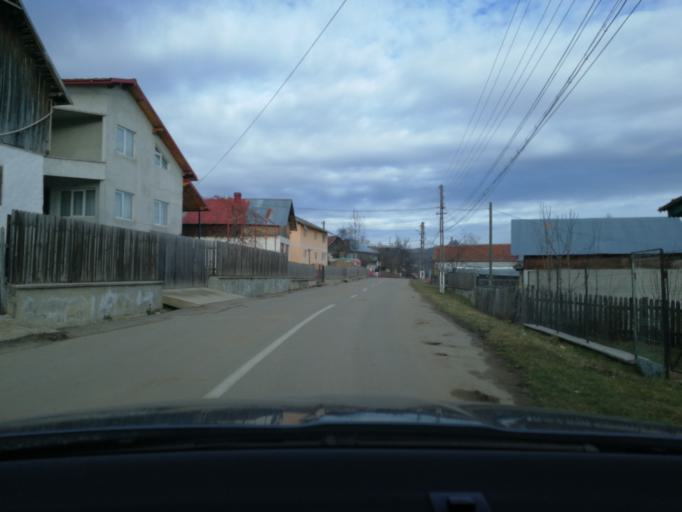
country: RO
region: Prahova
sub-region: Comuna Adunati
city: Ocina de Sus
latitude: 45.1806
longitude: 25.5901
